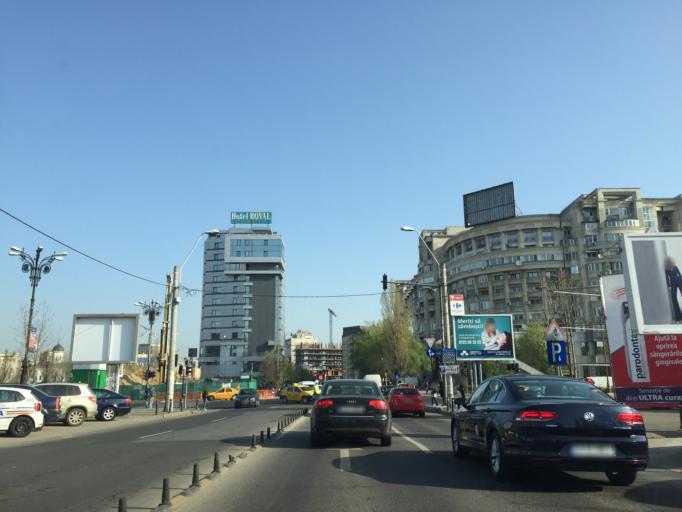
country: RO
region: Bucuresti
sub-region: Municipiul Bucuresti
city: Bucharest
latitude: 44.4258
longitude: 26.1120
